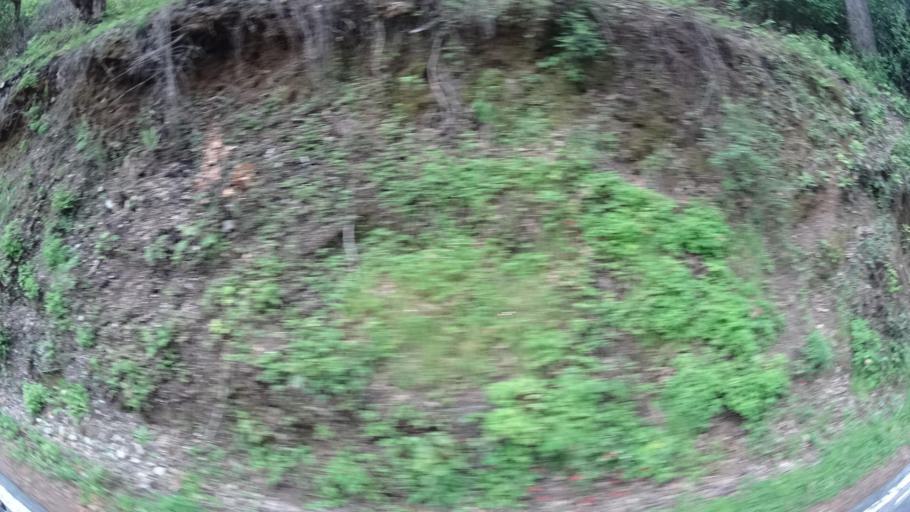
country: US
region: California
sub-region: Humboldt County
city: Willow Creek
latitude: 41.1973
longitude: -123.7287
